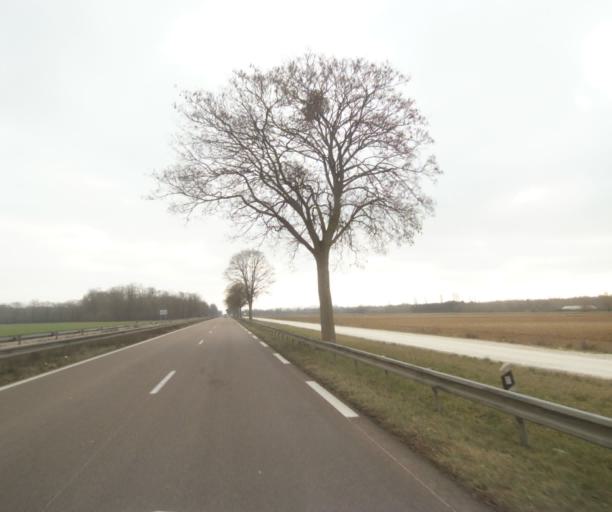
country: FR
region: Champagne-Ardenne
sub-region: Departement de la Marne
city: Pargny-sur-Saulx
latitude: 48.6765
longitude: 4.7606
